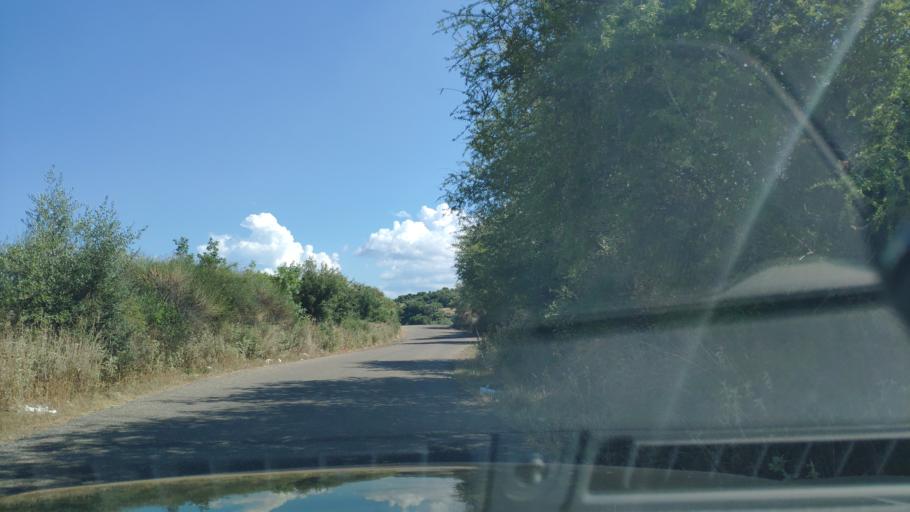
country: GR
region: West Greece
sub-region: Nomos Aitolias kai Akarnanias
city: Katouna
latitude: 38.8002
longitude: 21.1128
